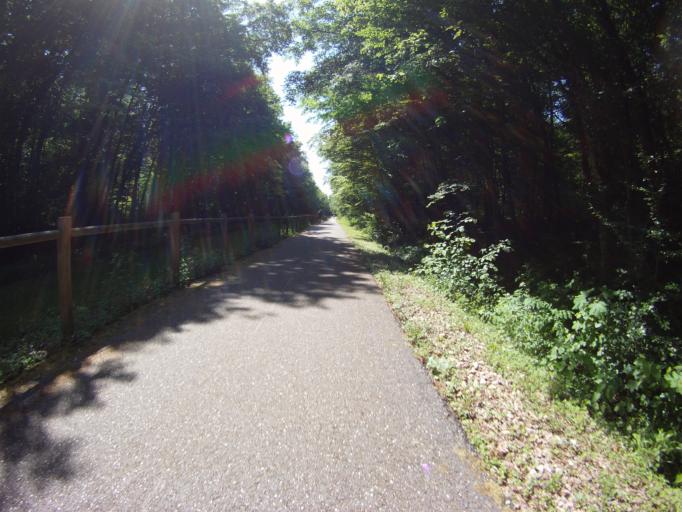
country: FR
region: Lorraine
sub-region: Departement de Meurthe-et-Moselle
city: Champenoux
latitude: 48.7512
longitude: 6.3244
